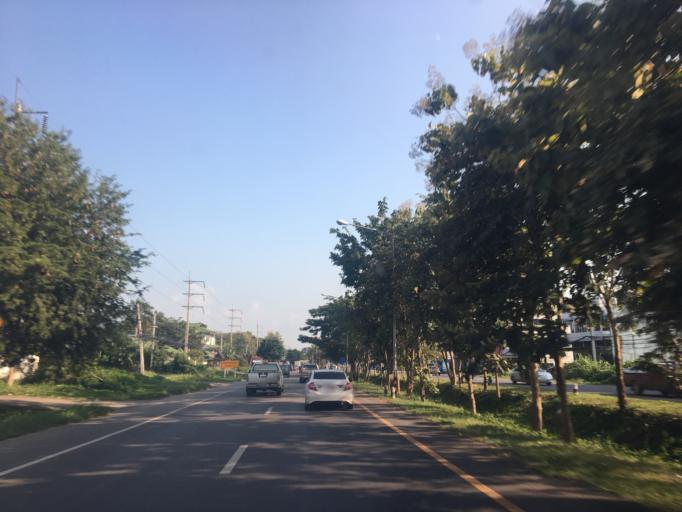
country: TH
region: Phayao
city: Phayao
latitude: 19.1680
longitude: 99.9092
